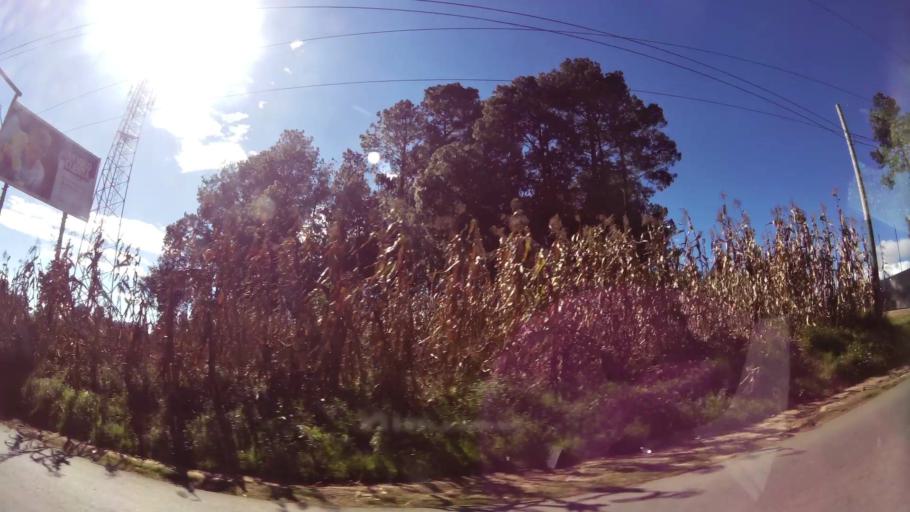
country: GT
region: Solola
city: Solola
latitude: 14.8074
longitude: -91.1797
